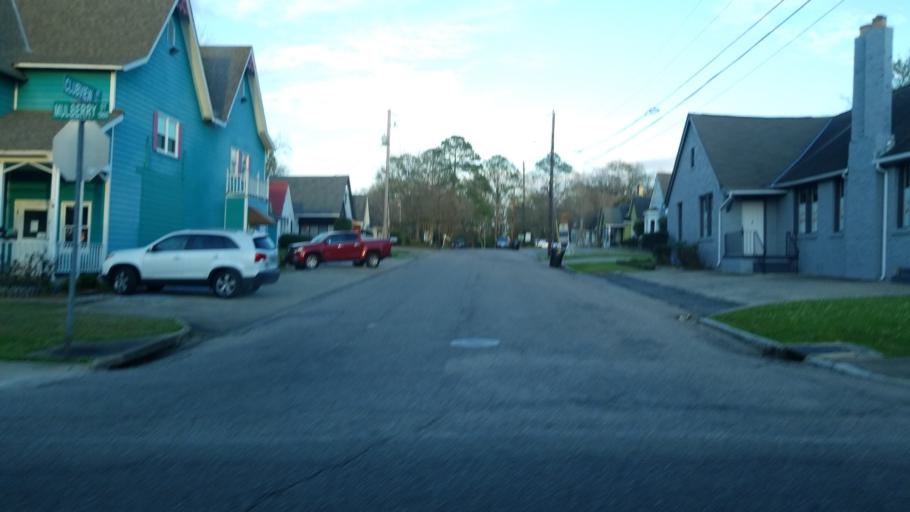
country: US
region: Alabama
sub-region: Montgomery County
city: Montgomery
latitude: 32.3596
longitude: -86.2833
